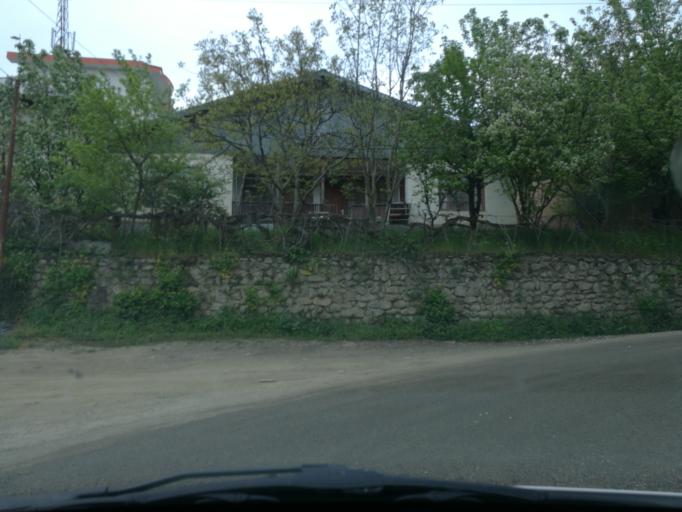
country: IR
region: Mazandaran
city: Chalus
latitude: 36.5316
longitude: 51.2299
